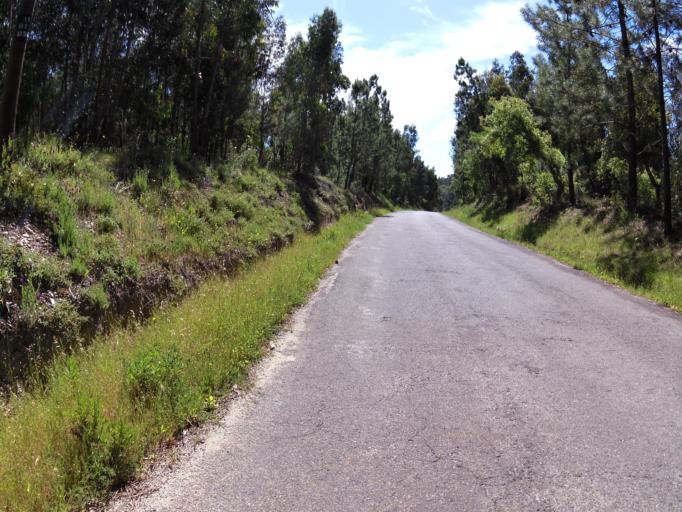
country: PT
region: Setubal
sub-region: Sines
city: Porto Covo
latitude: 37.9358
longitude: -8.7632
